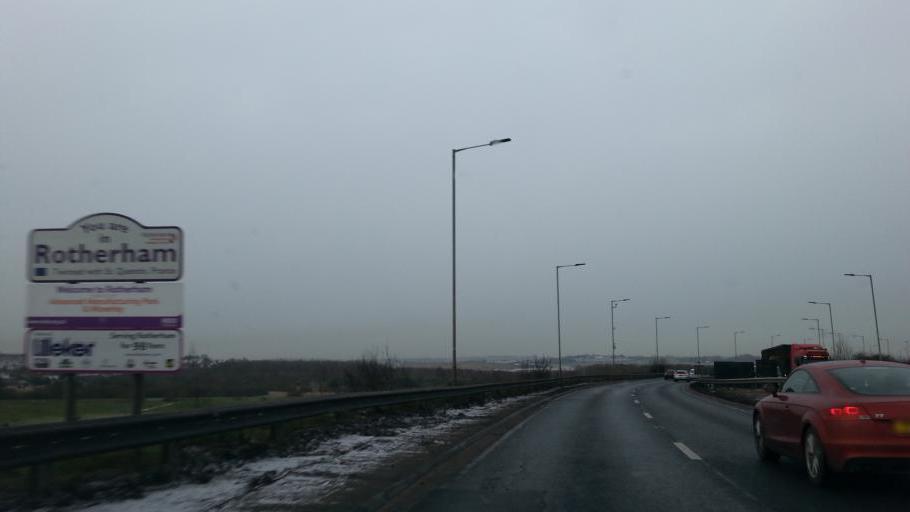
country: GB
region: England
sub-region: Rotherham
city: Treeton
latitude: 53.3976
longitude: -1.3491
